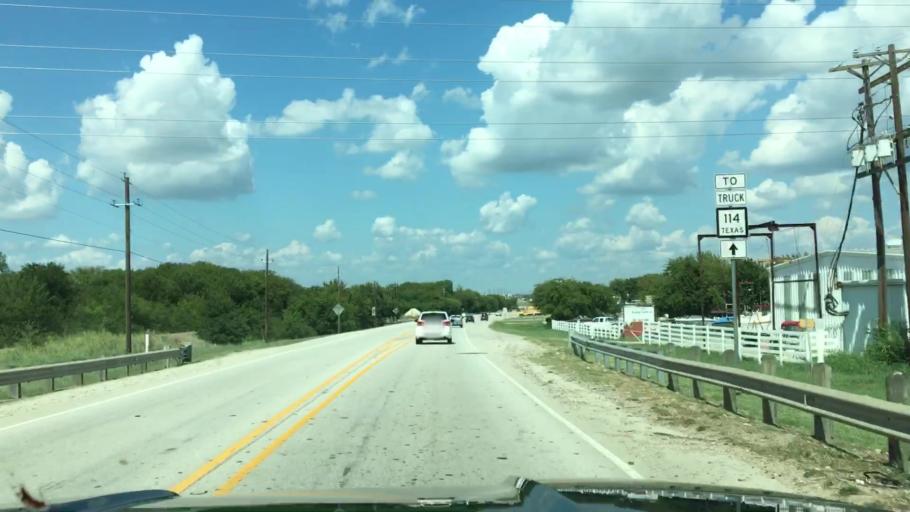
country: US
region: Texas
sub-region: Denton County
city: Roanoke
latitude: 33.0049
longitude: -97.2272
